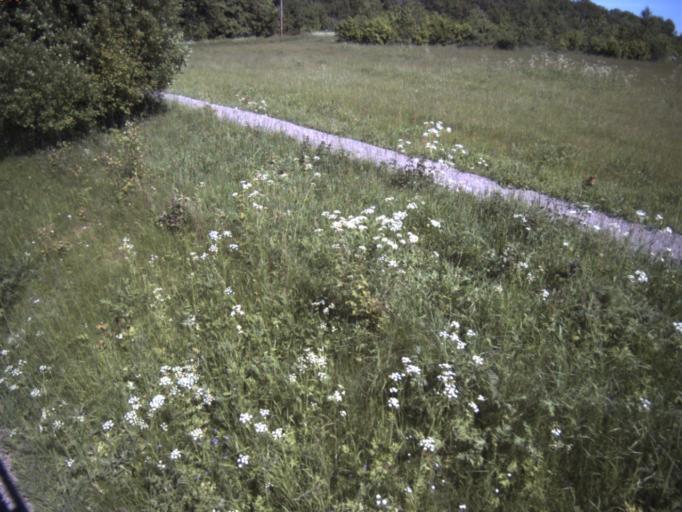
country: SE
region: Skane
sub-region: Helsingborg
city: Gantofta
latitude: 55.9980
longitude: 12.7847
